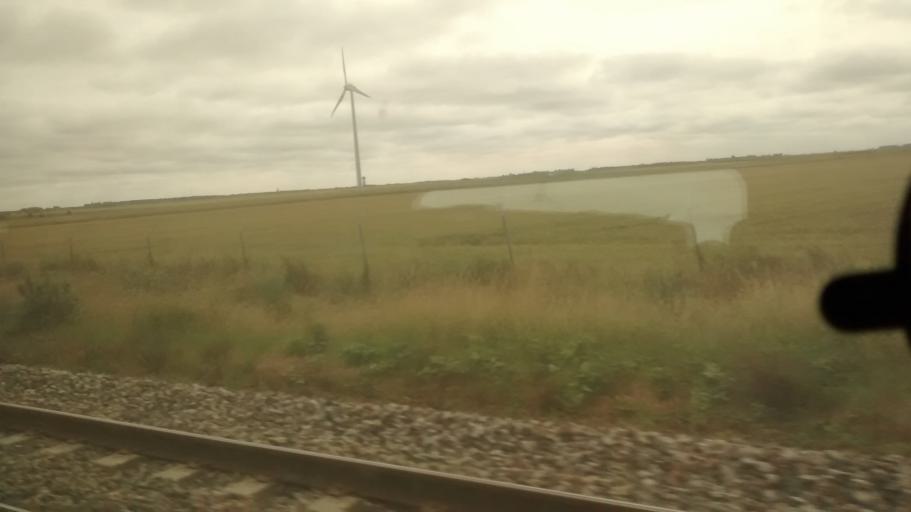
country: FR
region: Centre
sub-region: Departement d'Eure-et-Loir
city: Auneau
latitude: 48.4325
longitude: 1.7685
